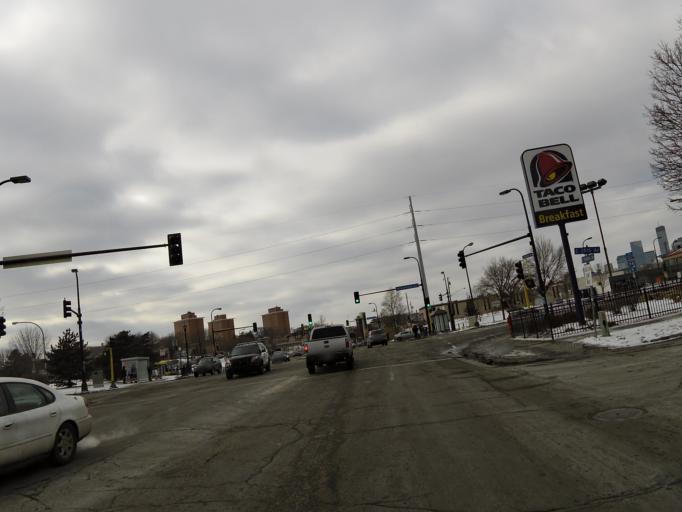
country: US
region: Minnesota
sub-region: Hennepin County
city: Minneapolis
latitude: 44.9628
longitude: -93.2440
